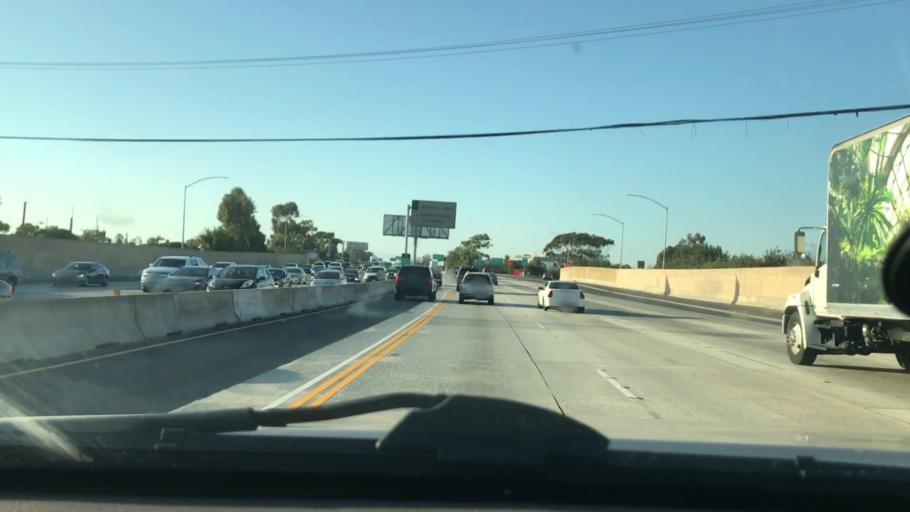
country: US
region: California
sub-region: Los Angeles County
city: Lawndale
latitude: 33.8823
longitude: -118.3494
